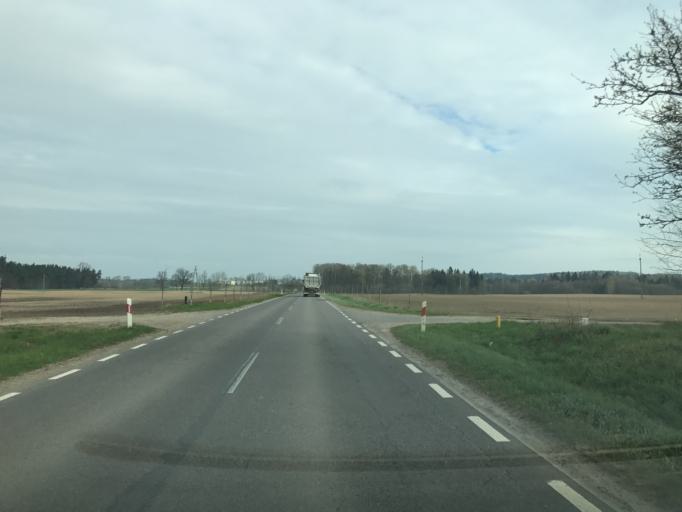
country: PL
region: Warmian-Masurian Voivodeship
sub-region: Powiat ostrodzki
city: Gierzwald
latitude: 53.5274
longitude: 20.0891
